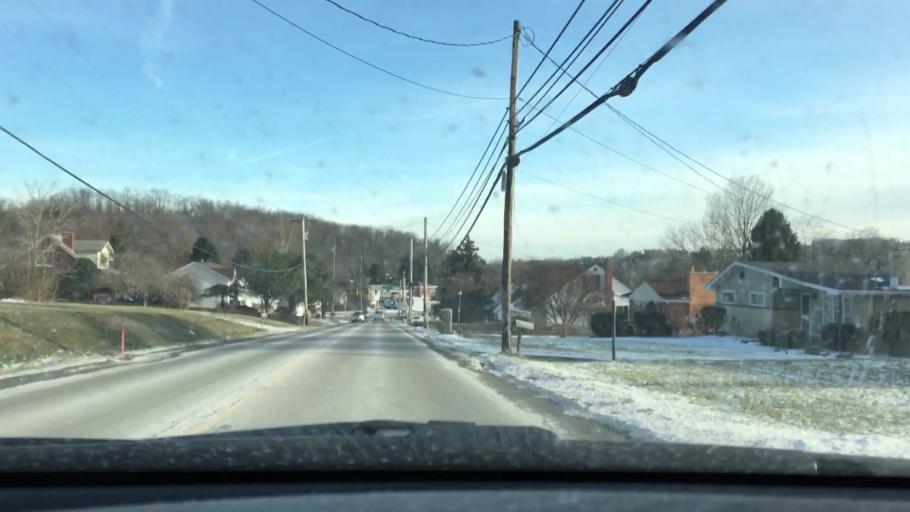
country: US
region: Pennsylvania
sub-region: Washington County
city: Gastonville
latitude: 40.2642
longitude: -80.0042
